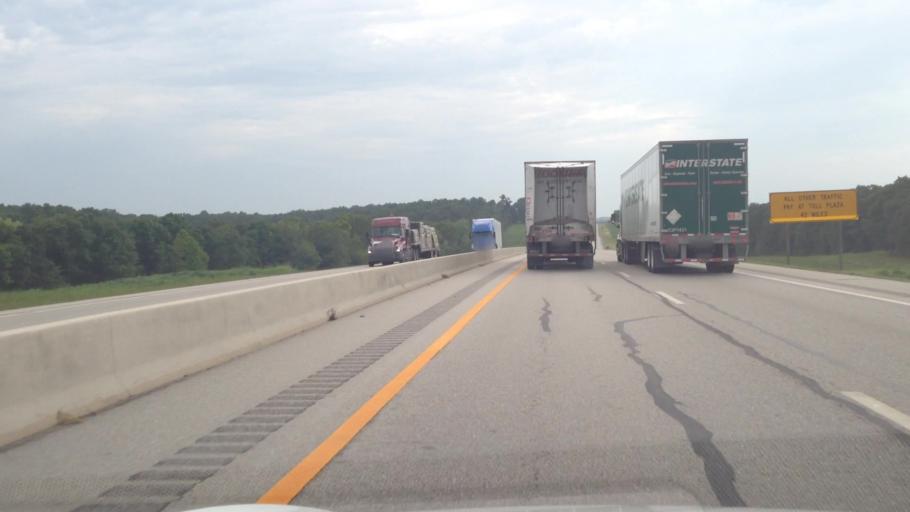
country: US
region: Kansas
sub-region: Cherokee County
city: Galena
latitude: 36.9797
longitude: -94.6382
